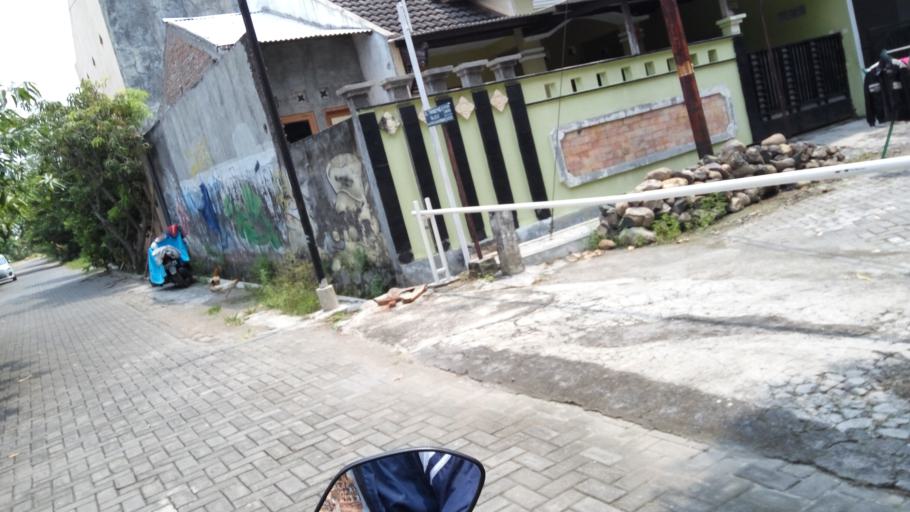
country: ID
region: Central Java
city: Mranggen
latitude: -7.0391
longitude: 110.4782
